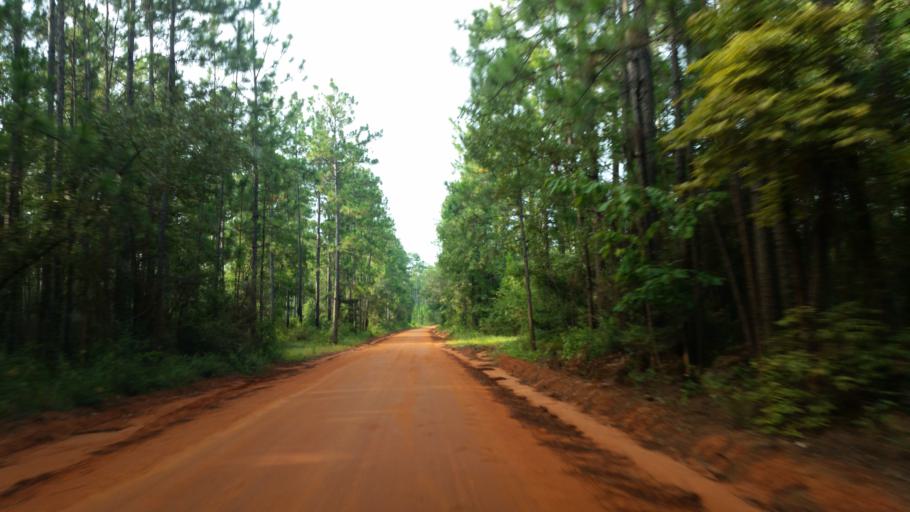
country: US
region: Alabama
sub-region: Escambia County
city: Atmore
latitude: 30.8862
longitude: -87.5825
